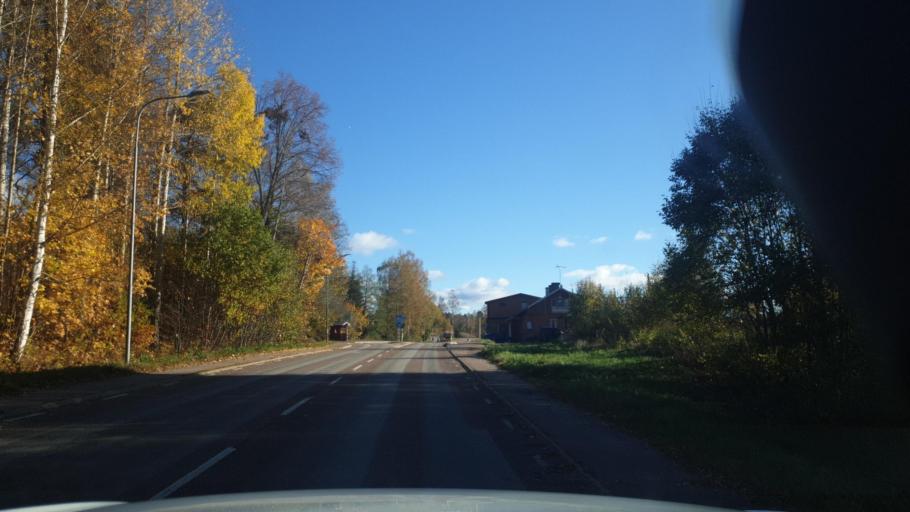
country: SE
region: Vaermland
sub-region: Arvika Kommun
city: Arvika
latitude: 59.6277
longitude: 12.8282
